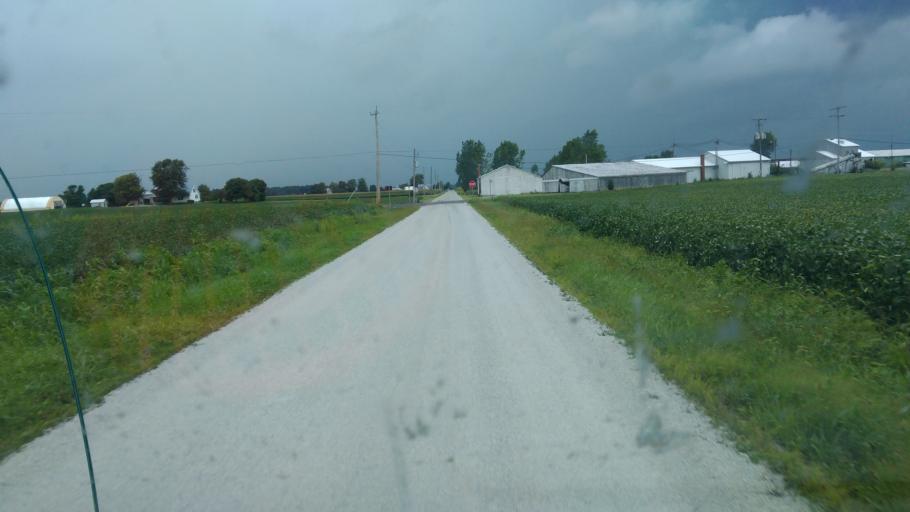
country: US
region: Ohio
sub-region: Hardin County
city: Kenton
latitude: 40.6790
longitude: -83.5145
